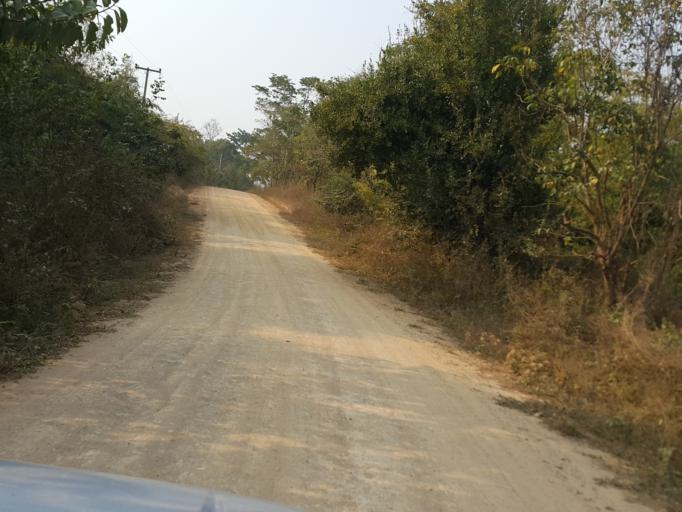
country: TH
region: Lamphun
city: Li
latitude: 17.5983
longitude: 98.9730
